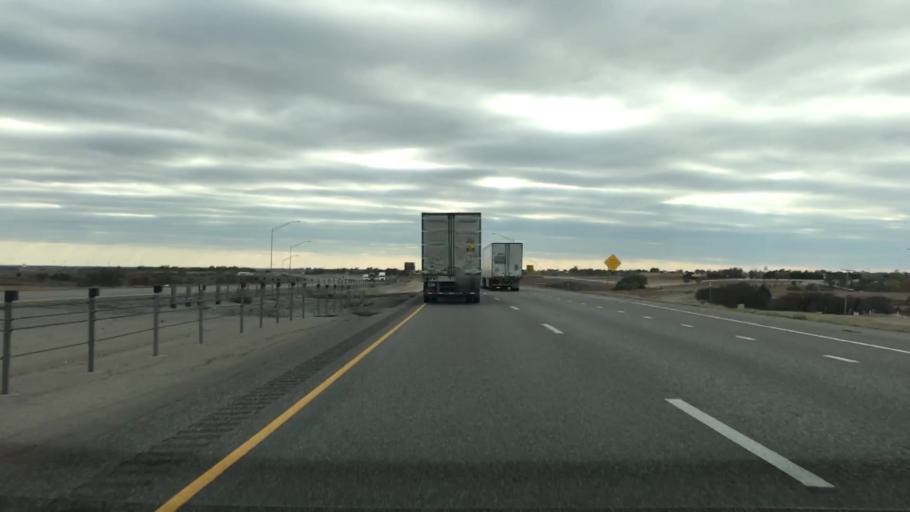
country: US
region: Oklahoma
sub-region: Beckham County
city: Sayre
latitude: 35.3197
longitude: -99.6102
